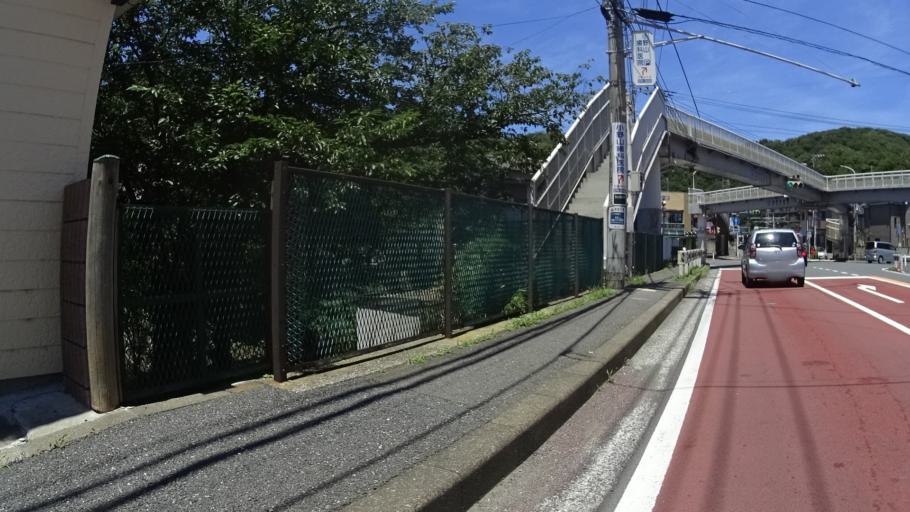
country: JP
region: Kanagawa
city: Hayama
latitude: 35.2825
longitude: 139.5798
